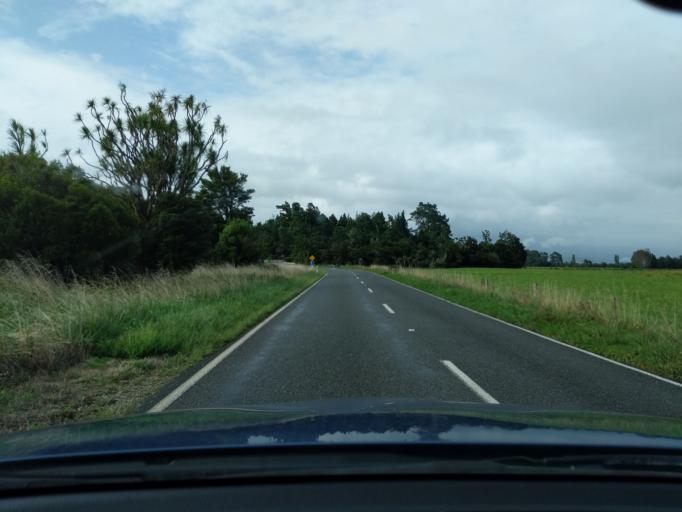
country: NZ
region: Tasman
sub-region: Tasman District
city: Takaka
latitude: -40.6586
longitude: 172.6468
